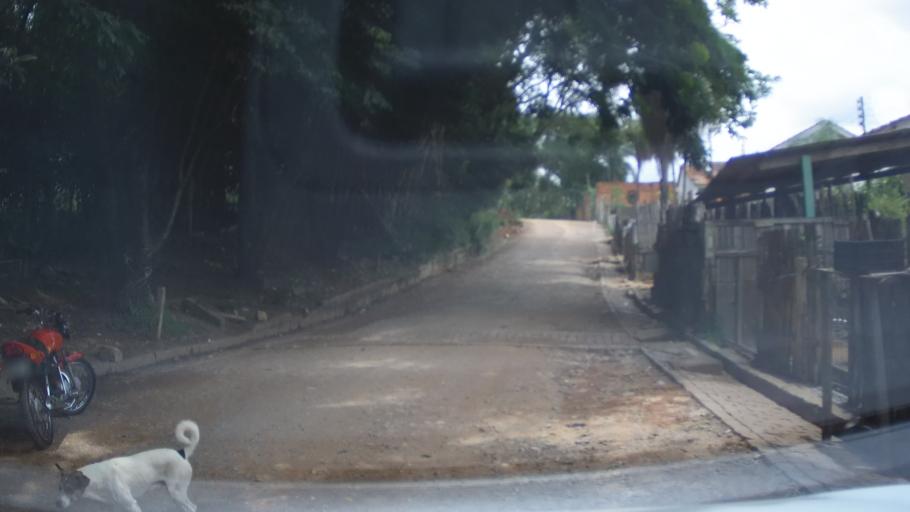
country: BR
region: Sao Paulo
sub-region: Vinhedo
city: Vinhedo
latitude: -23.0022
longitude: -46.9570
